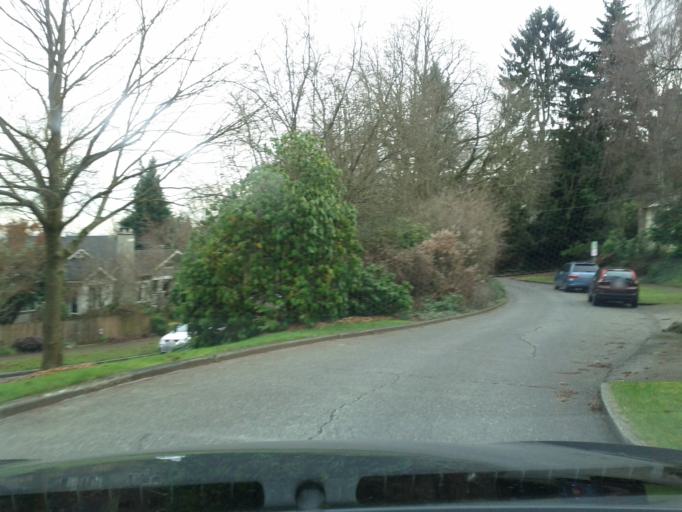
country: US
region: Washington
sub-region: King County
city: Seattle
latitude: 47.6703
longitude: -122.3080
